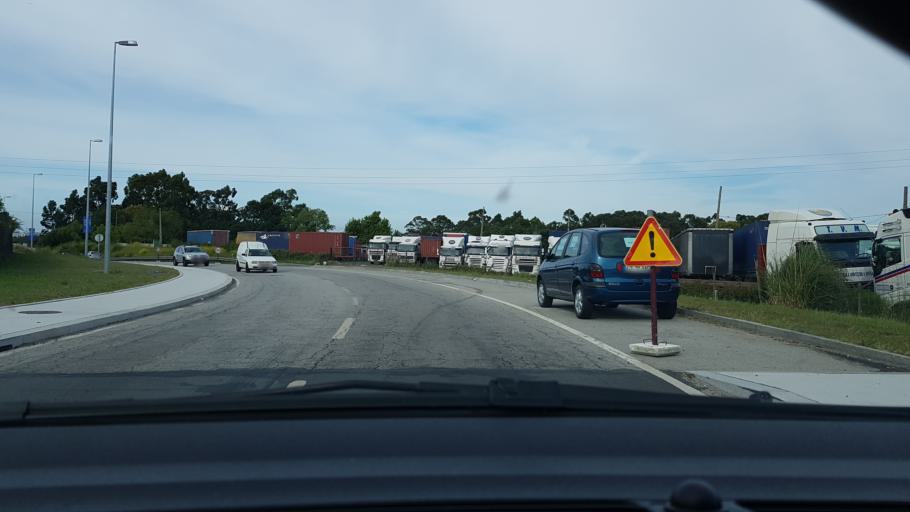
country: PT
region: Porto
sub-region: Maia
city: Leca do Bailio
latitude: 41.2084
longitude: -8.6325
